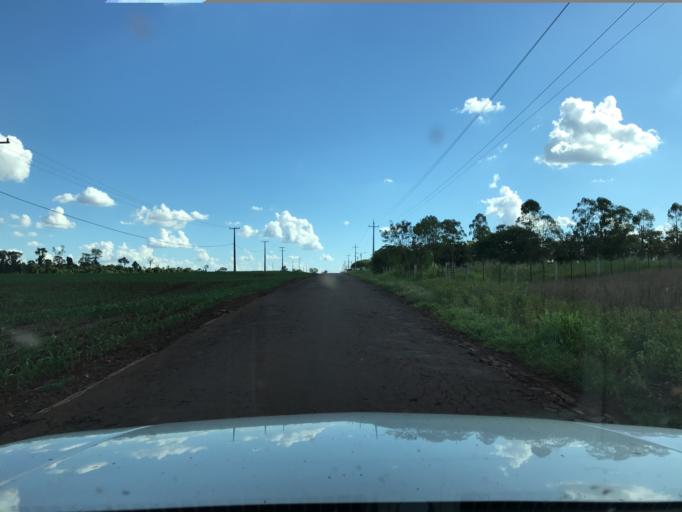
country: BR
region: Parana
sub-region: Palotina
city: Palotina
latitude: -24.2689
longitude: -53.8055
